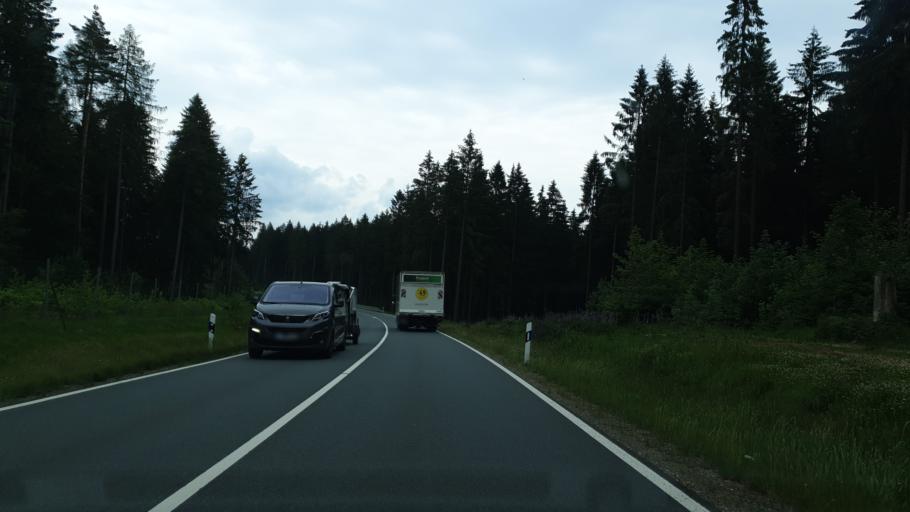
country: DE
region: Saxony
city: Tannenbergsthal
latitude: 50.4604
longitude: 12.4452
